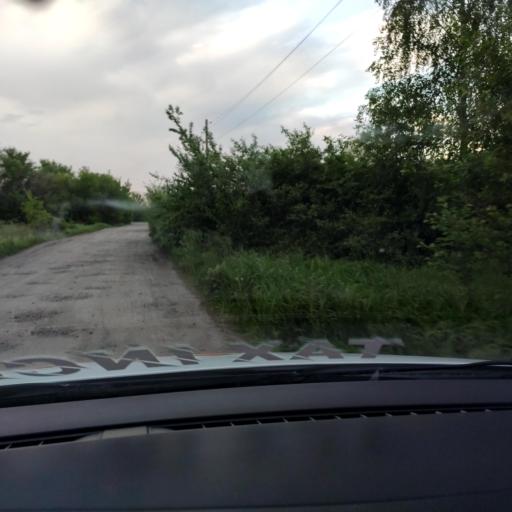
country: RU
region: Voronezj
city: Kolodeznyy
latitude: 51.4360
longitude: 39.2320
